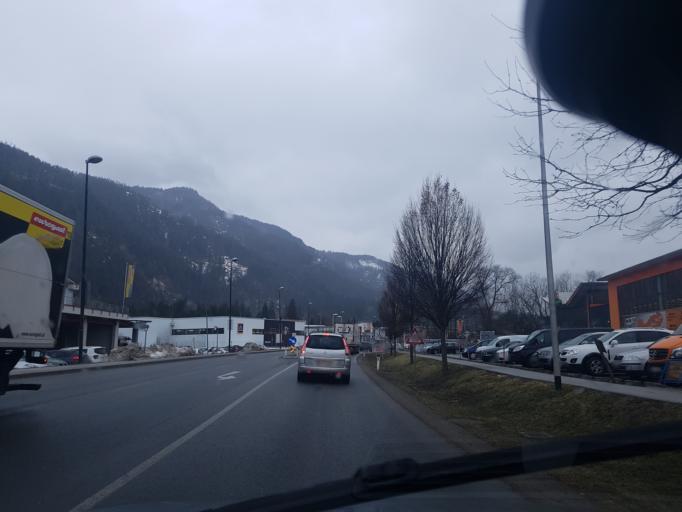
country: AT
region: Tyrol
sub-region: Politischer Bezirk Kufstein
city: Worgl
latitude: 47.4788
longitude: 12.0473
